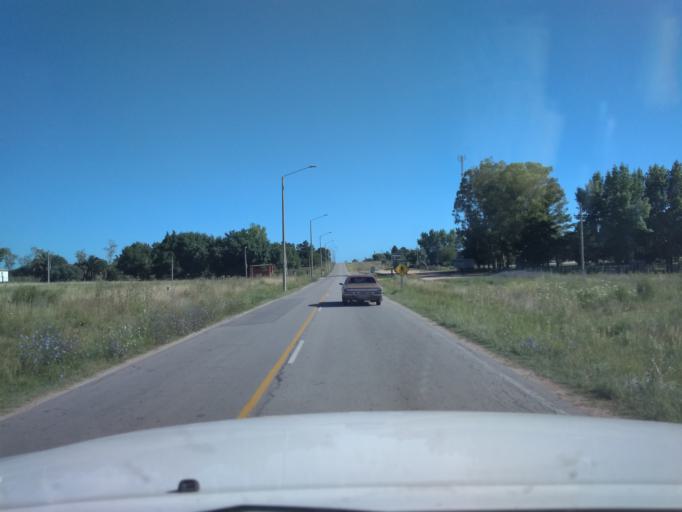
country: UY
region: Canelones
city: San Ramon
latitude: -34.3091
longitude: -55.9586
